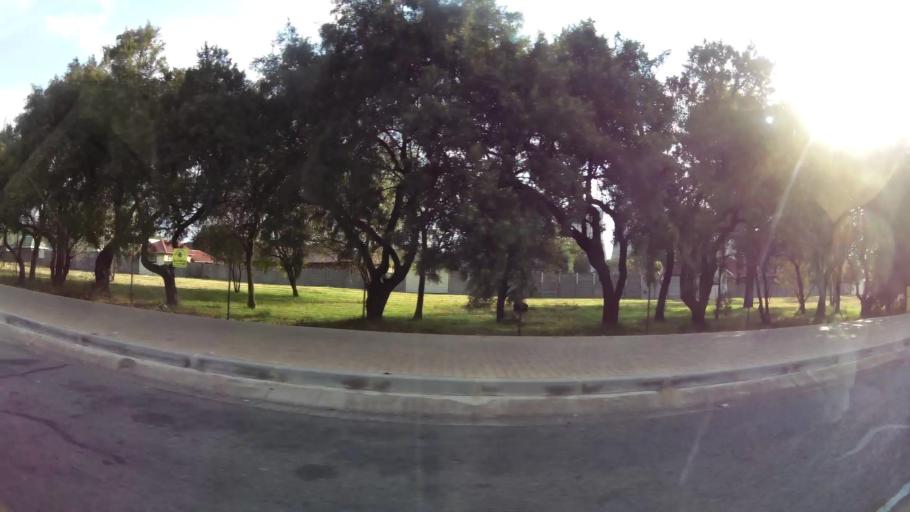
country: ZA
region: Gauteng
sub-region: City of Johannesburg Metropolitan Municipality
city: Modderfontein
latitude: -26.1196
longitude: 28.2000
